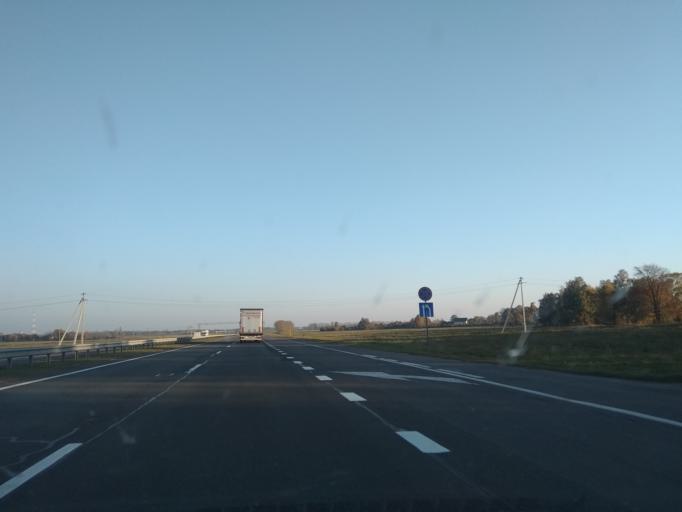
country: BY
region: Brest
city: Kobryn
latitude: 52.1937
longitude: 24.3057
